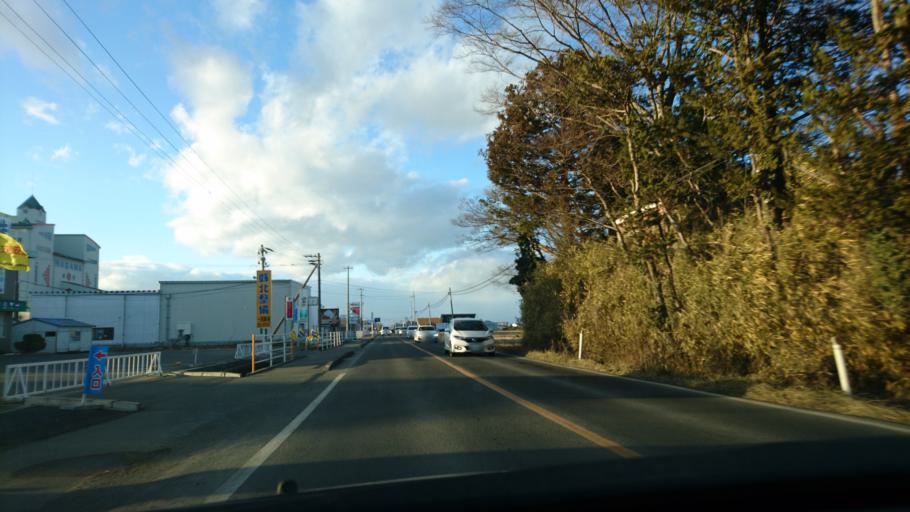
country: JP
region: Miyagi
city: Wakuya
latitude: 38.7090
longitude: 141.1795
